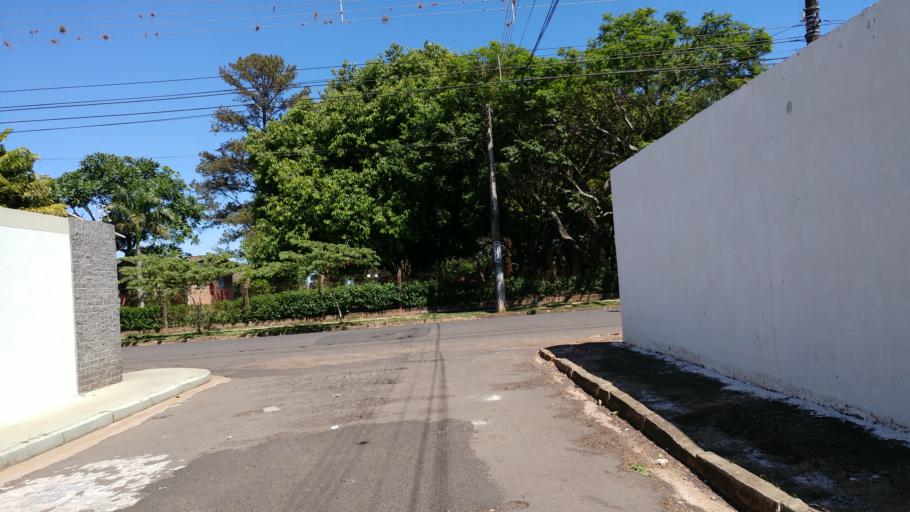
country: BR
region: Sao Paulo
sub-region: Paraguacu Paulista
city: Paraguacu Paulista
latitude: -22.4181
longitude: -50.5817
